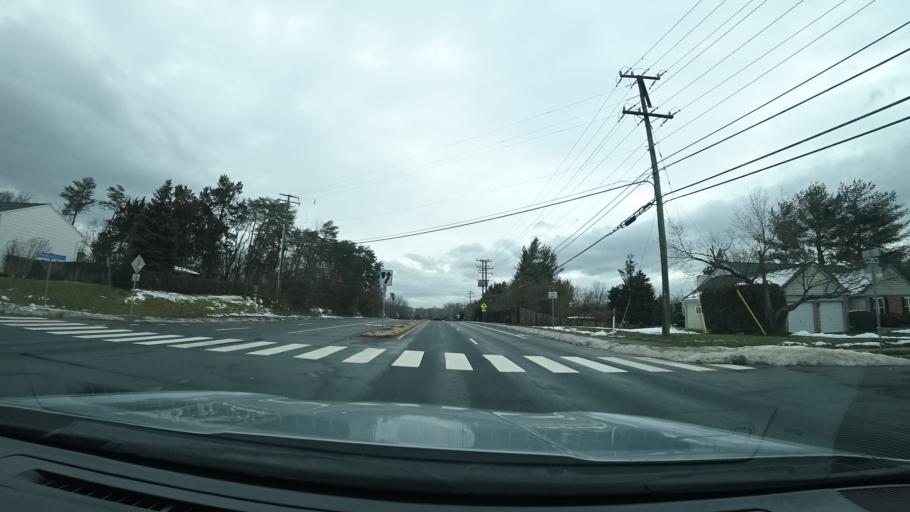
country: US
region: Virginia
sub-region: Fairfax County
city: Dranesville
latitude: 39.0024
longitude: -77.3755
